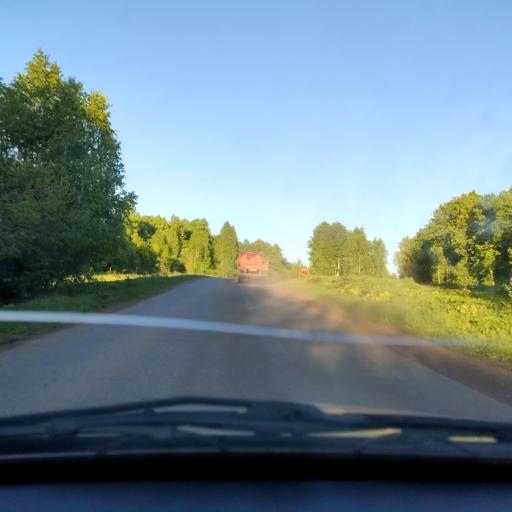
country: RU
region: Bashkortostan
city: Blagoveshchensk
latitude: 55.0333
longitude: 56.0919
